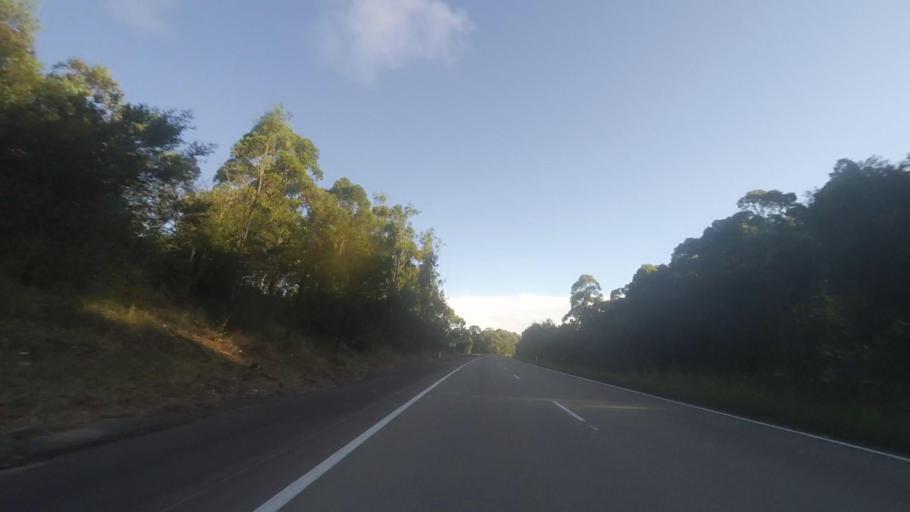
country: AU
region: New South Wales
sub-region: Great Lakes
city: Bulahdelah
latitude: -32.2974
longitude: 152.3455
